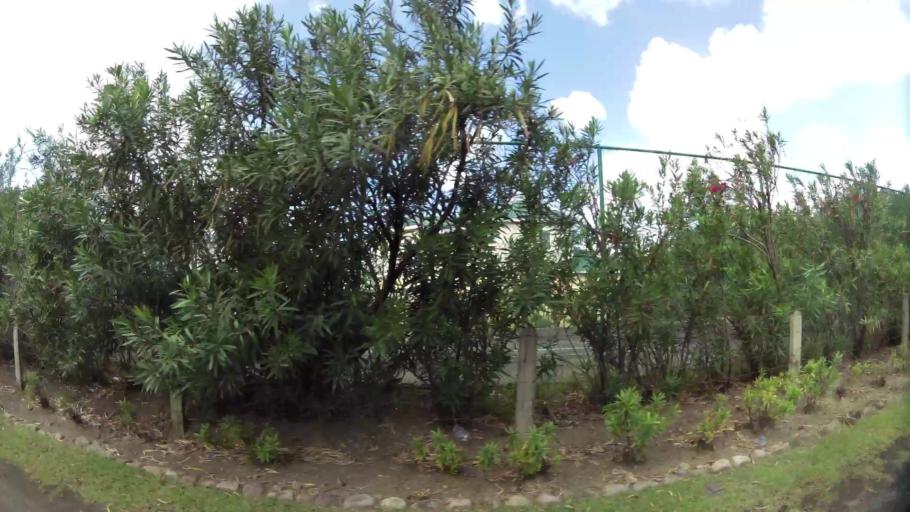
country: KN
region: Saint Thomas Lowland
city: Cotton Ground
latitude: 17.1772
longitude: -62.6235
